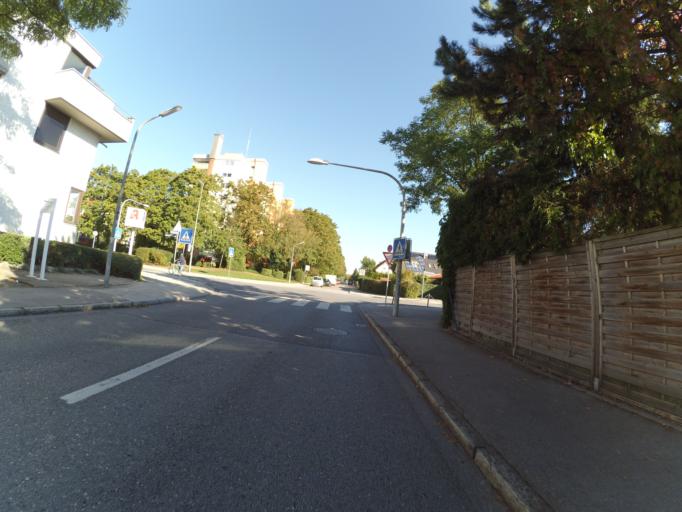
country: DE
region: Bavaria
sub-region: Upper Bavaria
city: Oberschleissheim
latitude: 48.2039
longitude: 11.5536
